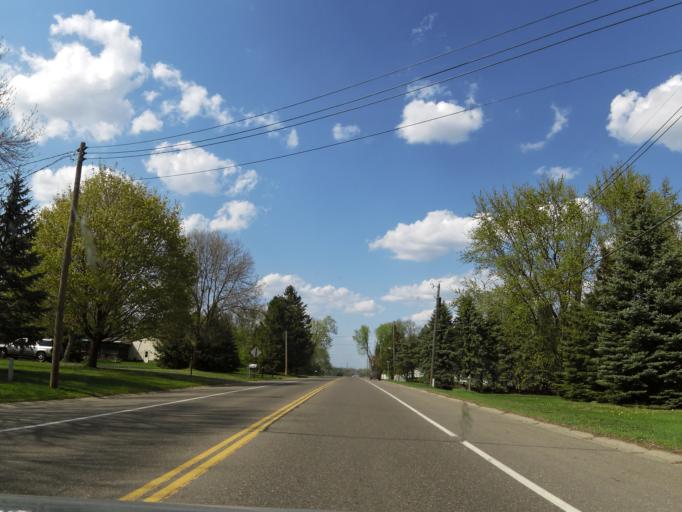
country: US
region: Minnesota
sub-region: Washington County
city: Oak Park Heights
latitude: 45.0197
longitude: -92.8071
